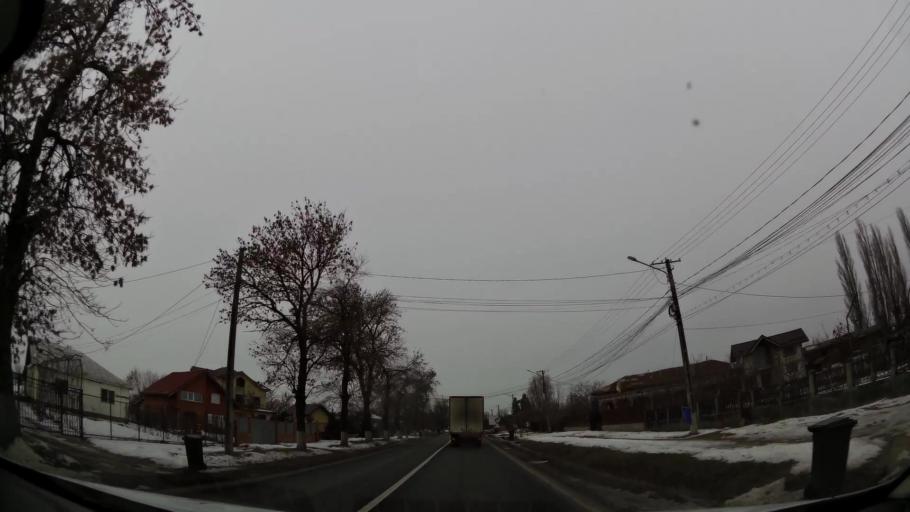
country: RO
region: Dambovita
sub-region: Comuna Tartasesti
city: Baldana
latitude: 44.6030
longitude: 25.7754
